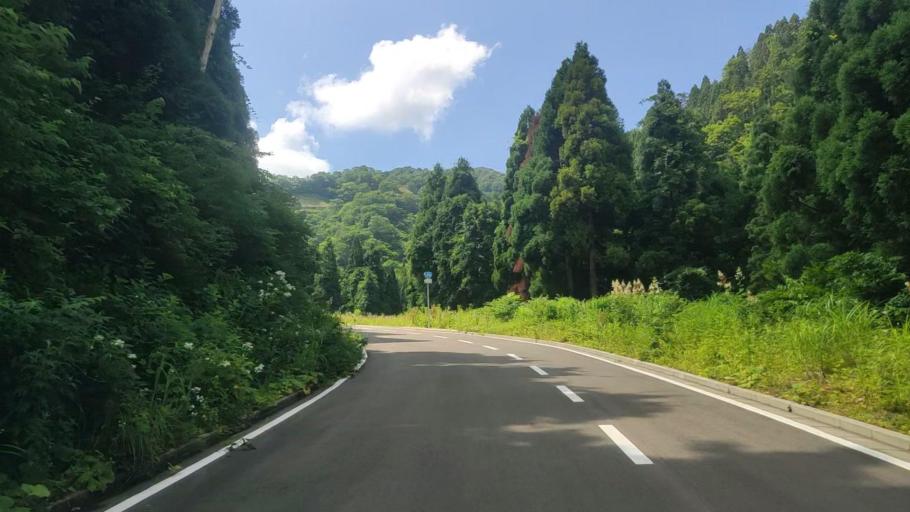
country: JP
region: Fukui
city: Katsuyama
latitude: 36.1568
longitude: 136.5264
